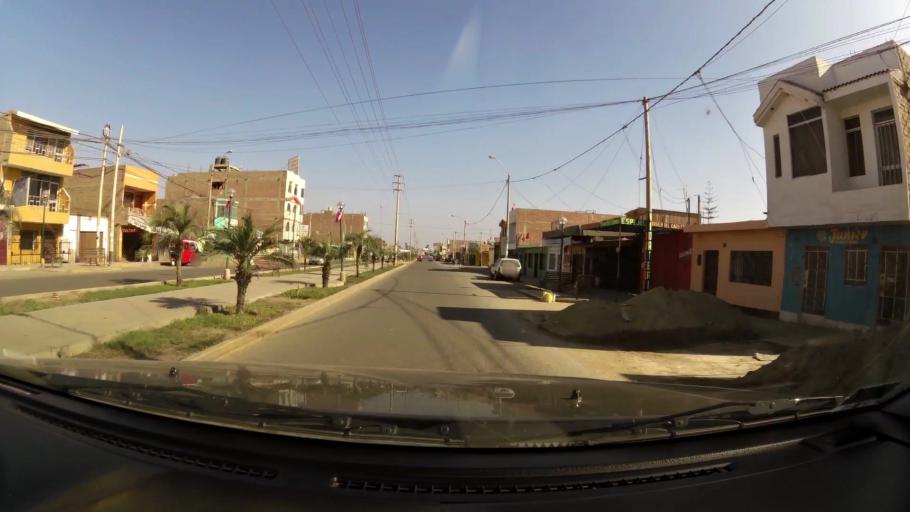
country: PE
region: Ica
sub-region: Provincia de Chincha
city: Chincha Alta
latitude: -13.4062
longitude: -76.1302
